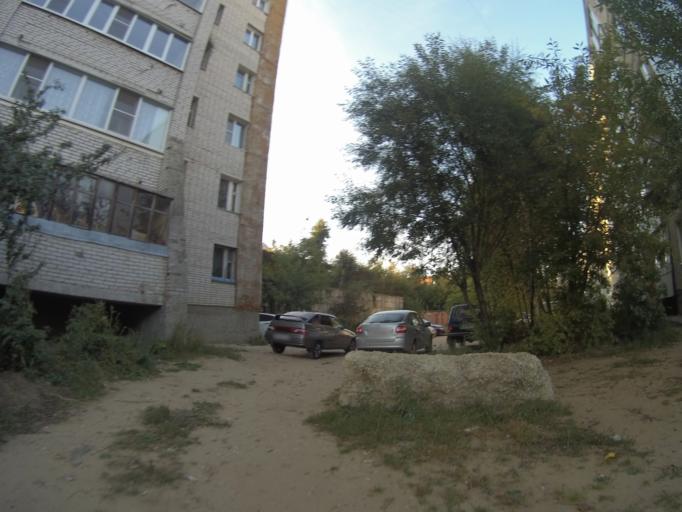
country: RU
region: Vladimir
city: Vladimir
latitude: 56.1123
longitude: 40.3781
